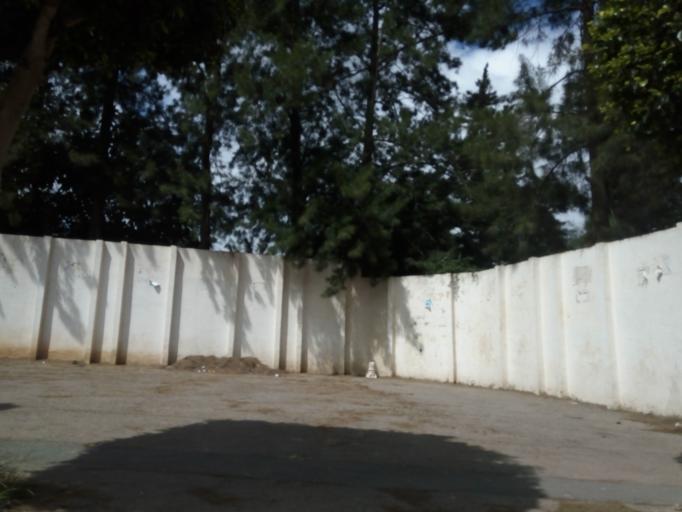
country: DZ
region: Tipaza
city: Douera
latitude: 36.6990
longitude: 2.9768
